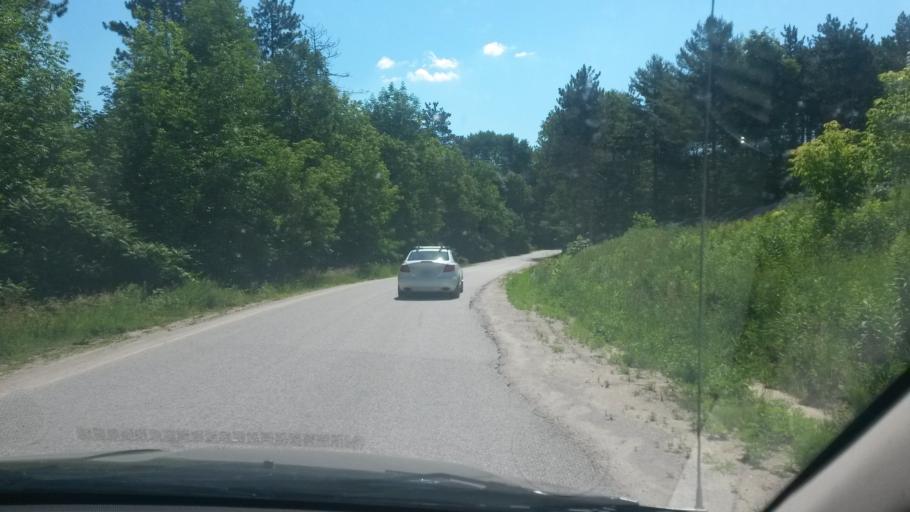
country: CA
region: Ontario
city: Barrie
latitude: 44.5522
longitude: -79.6783
